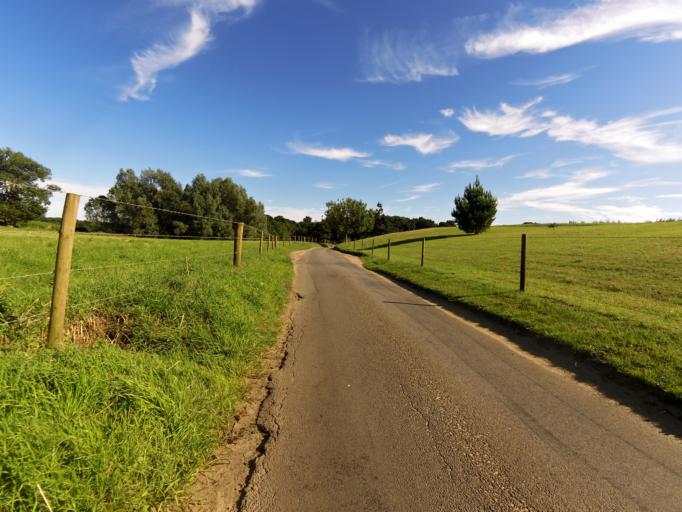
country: GB
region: England
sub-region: Suffolk
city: Kesgrave
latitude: 52.0455
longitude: 1.2518
